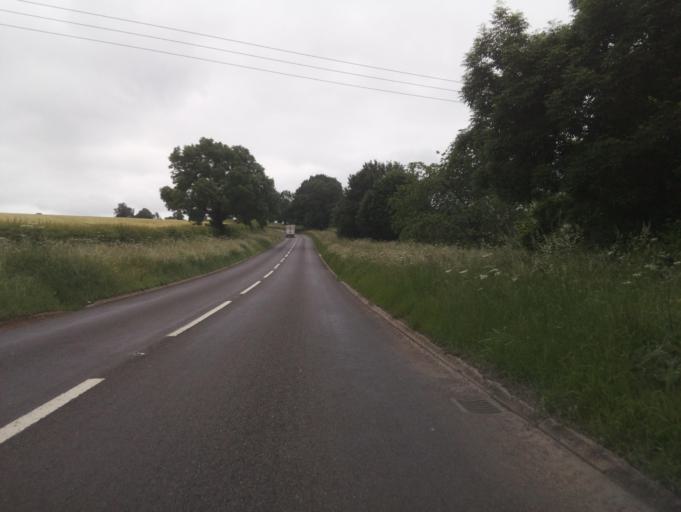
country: GB
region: England
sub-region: District of Rutland
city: Preston
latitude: 52.6039
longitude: -0.7207
